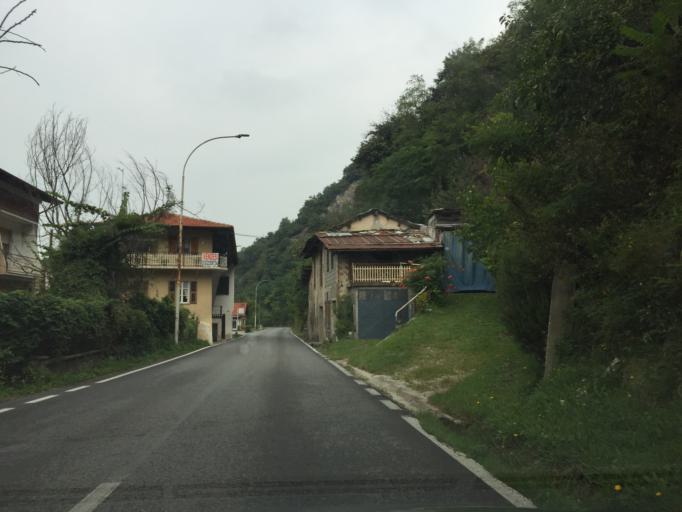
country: IT
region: Piedmont
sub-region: Provincia di Cuneo
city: Chiusa di Pesio
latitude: 44.3227
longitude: 7.6828
